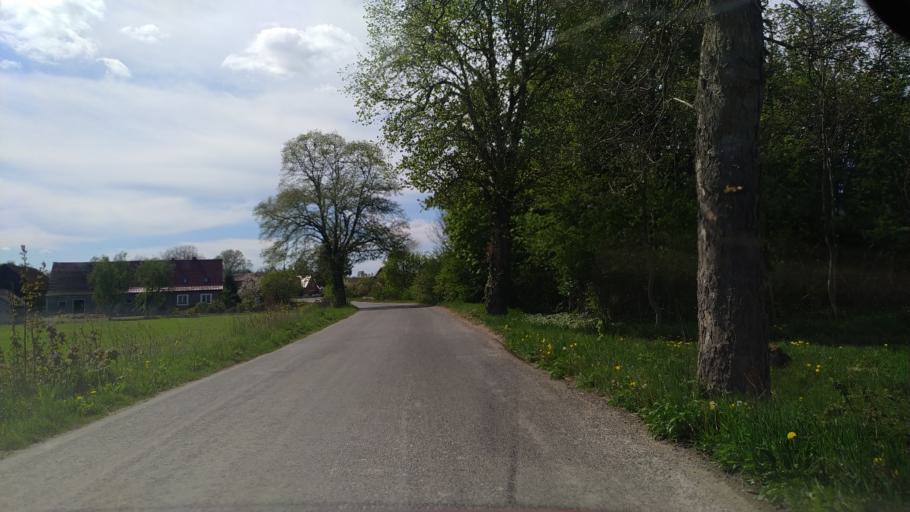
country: PL
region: West Pomeranian Voivodeship
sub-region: Powiat walecki
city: Walcz
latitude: 53.3528
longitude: 16.3362
